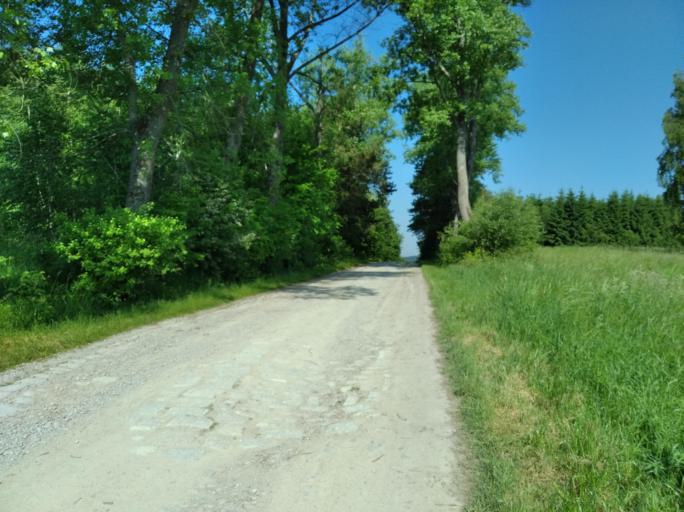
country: PL
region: Subcarpathian Voivodeship
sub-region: Powiat krosnienski
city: Odrzykon
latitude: 49.7672
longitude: 21.7811
